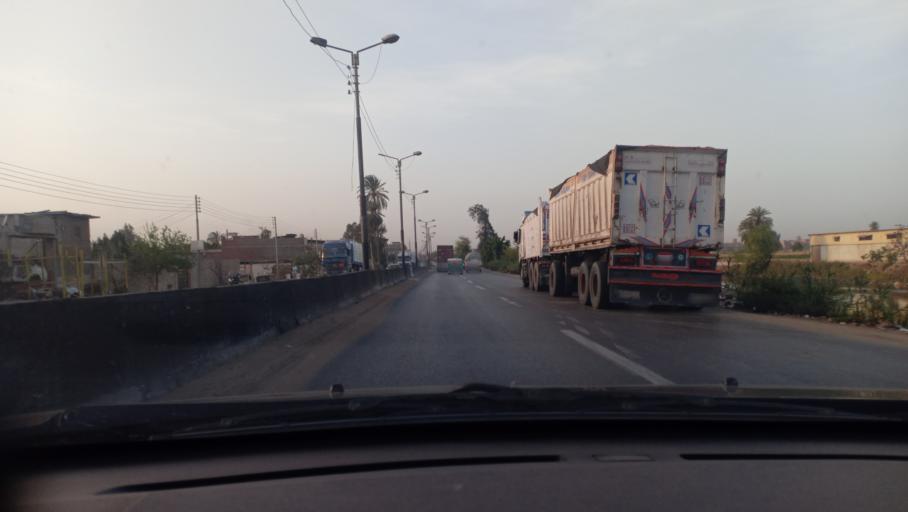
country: EG
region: Muhafazat al Gharbiyah
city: Zifta
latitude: 30.6577
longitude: 31.2842
